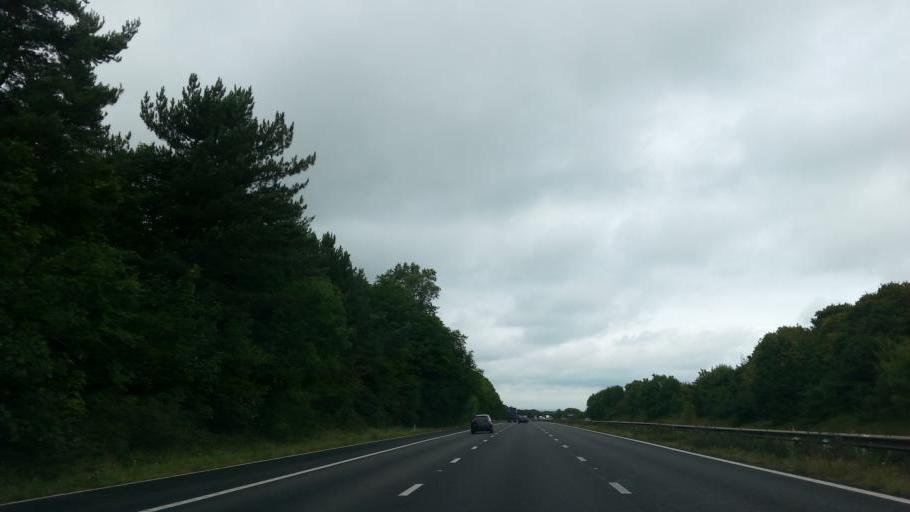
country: GB
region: England
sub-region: Leicestershire
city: Cosby
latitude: 52.5365
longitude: -1.1801
